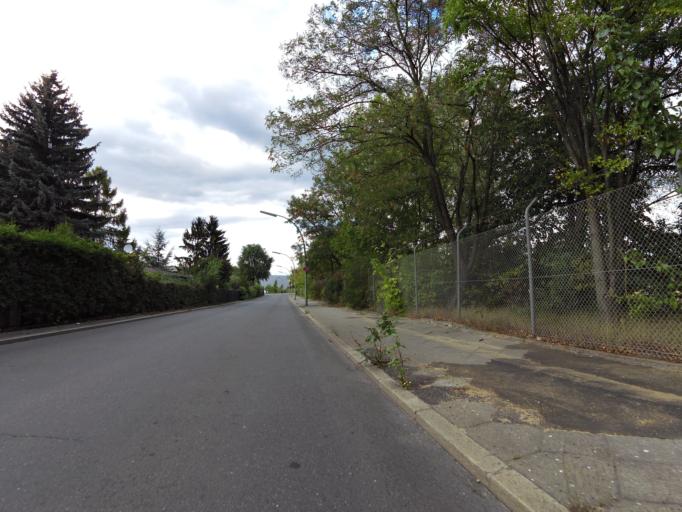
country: DE
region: Berlin
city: Altglienicke
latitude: 52.4227
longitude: 13.5149
